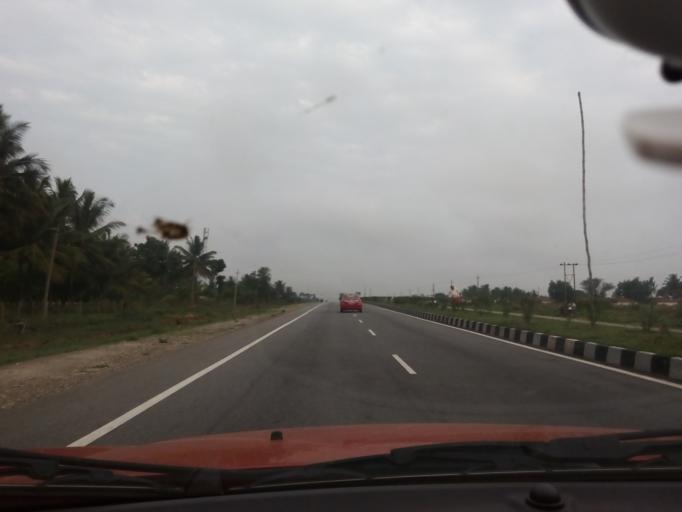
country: IN
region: Karnataka
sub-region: Mandya
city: Belluru
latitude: 12.9627
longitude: 76.6502
